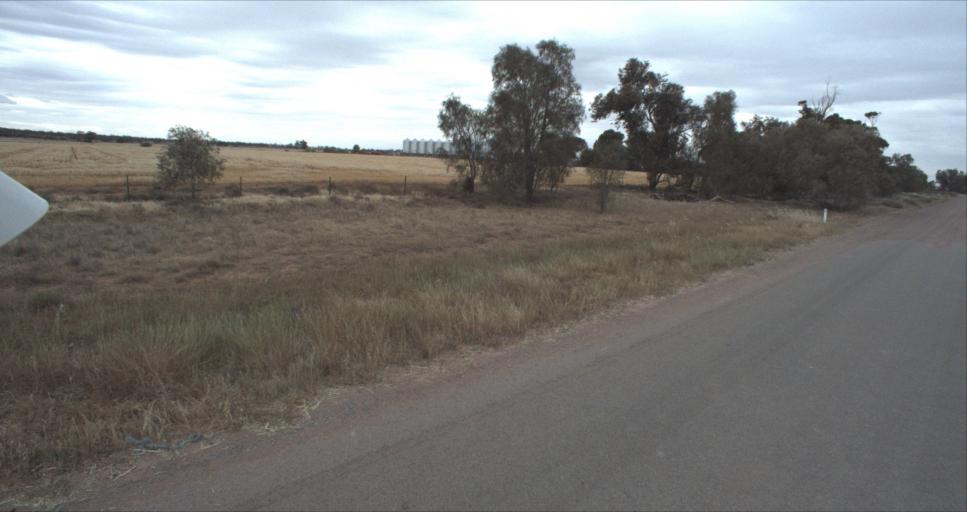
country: AU
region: New South Wales
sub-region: Leeton
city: Leeton
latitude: -34.4443
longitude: 146.3750
